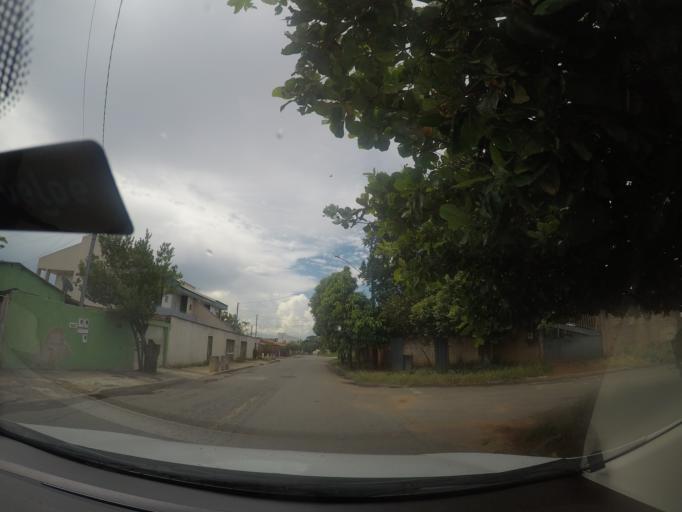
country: BR
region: Goias
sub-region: Goiania
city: Goiania
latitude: -16.7516
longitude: -49.3377
